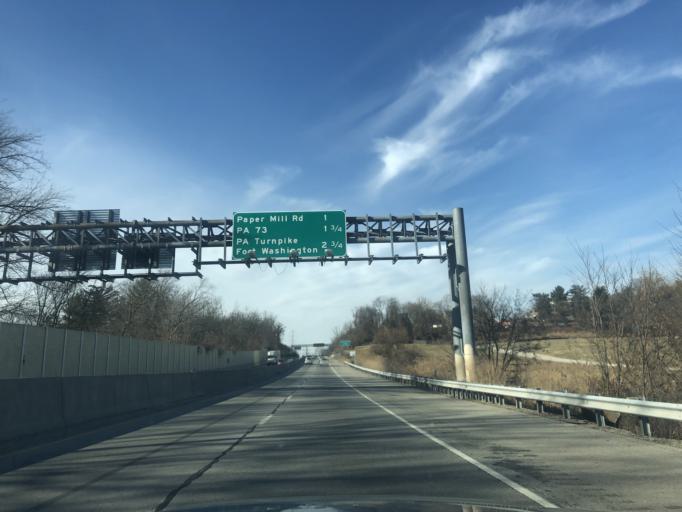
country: US
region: Pennsylvania
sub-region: Montgomery County
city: Wyndmoor
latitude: 40.0952
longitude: -75.1734
